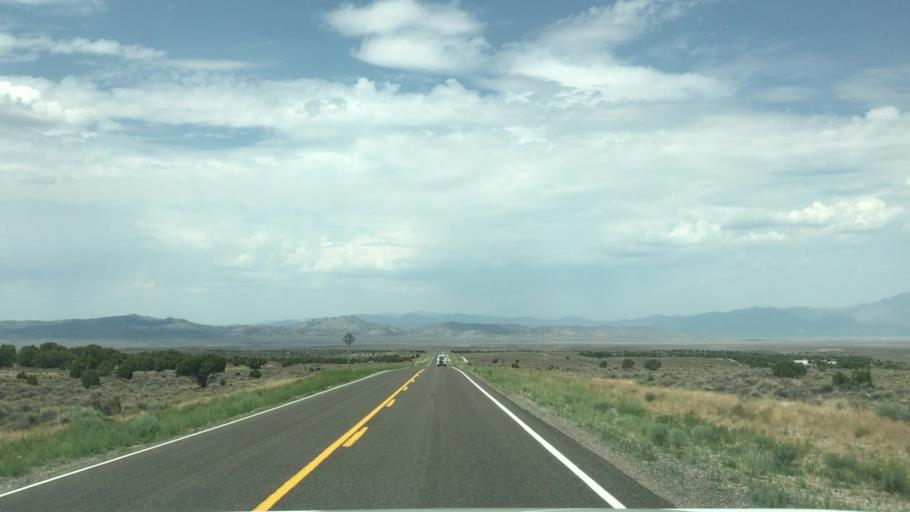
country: US
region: Nevada
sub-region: Eureka County
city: Eureka
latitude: 39.3921
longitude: -115.5101
